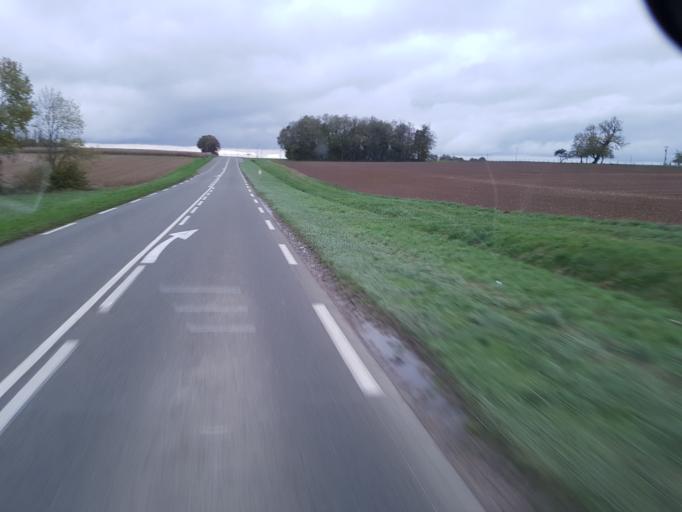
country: FR
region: Champagne-Ardenne
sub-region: Departement de la Marne
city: Montmirail
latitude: 48.8868
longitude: 3.5054
